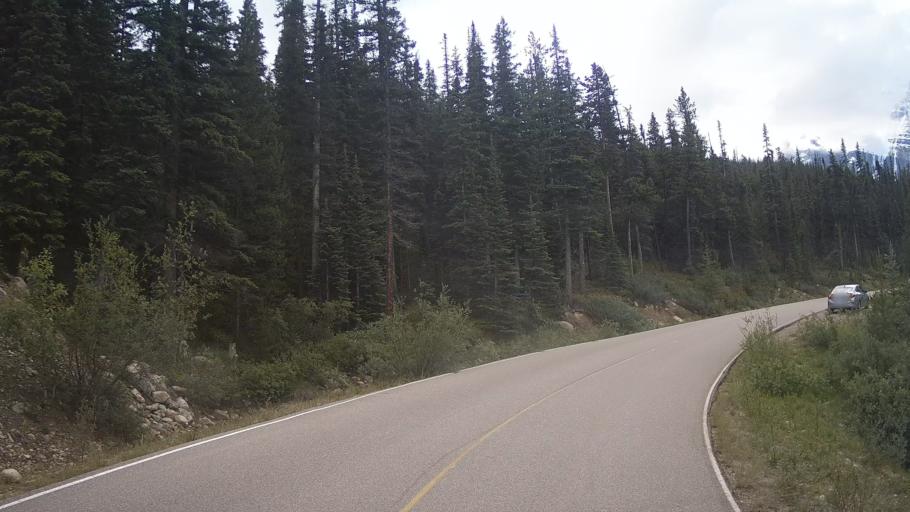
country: CA
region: Alberta
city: Jasper Park Lodge
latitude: 52.7145
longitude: -118.0550
